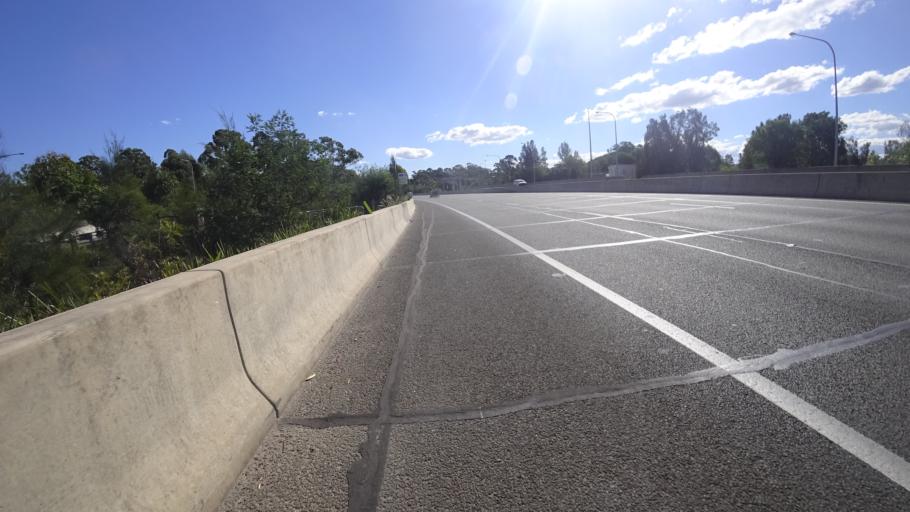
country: AU
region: New South Wales
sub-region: Ryde
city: Macquarie Park
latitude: -33.7742
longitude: 151.1227
